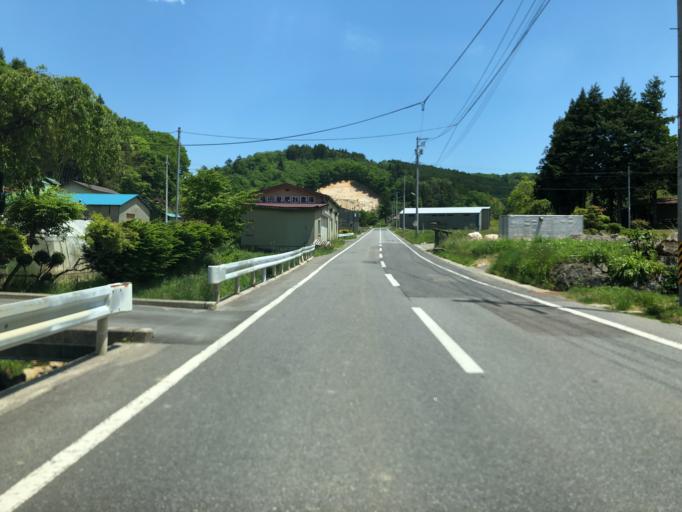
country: JP
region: Fukushima
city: Funehikimachi-funehiki
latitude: 37.5128
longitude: 140.6653
